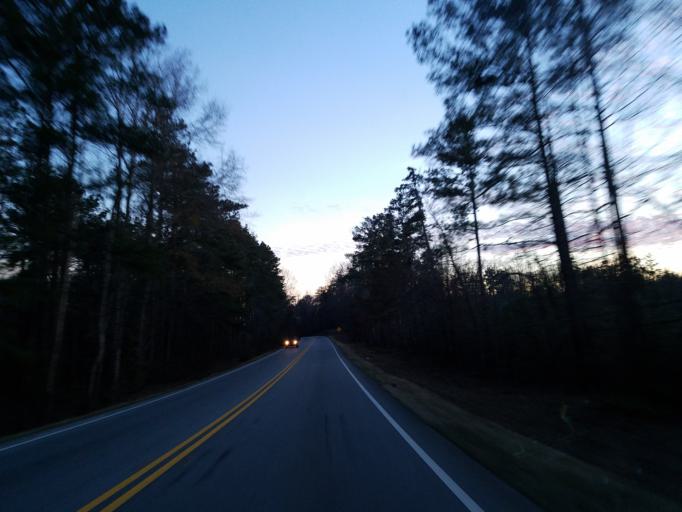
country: US
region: Georgia
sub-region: Paulding County
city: Dallas
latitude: 33.9720
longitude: -84.8609
